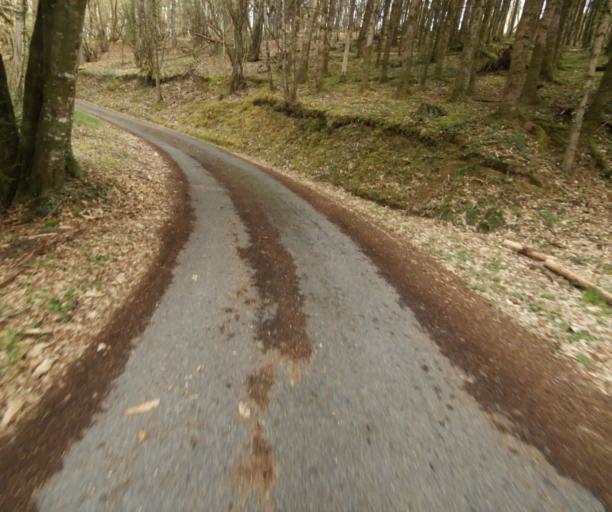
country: FR
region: Limousin
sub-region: Departement de la Correze
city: Naves
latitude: 45.3239
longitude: 1.8176
